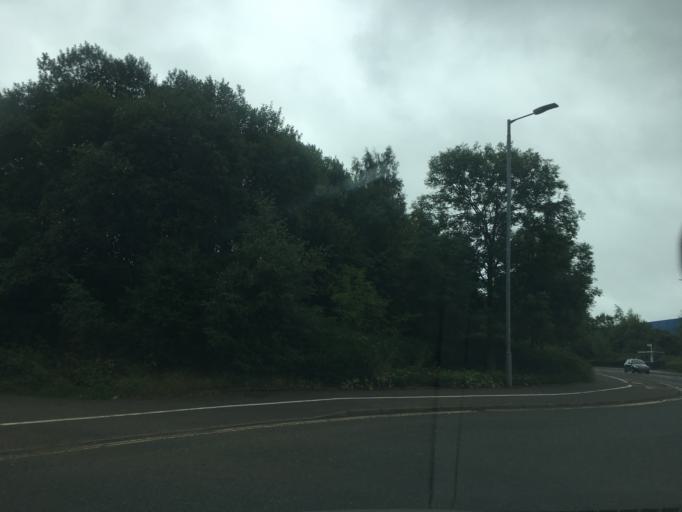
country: GB
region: Scotland
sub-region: Renfrewshire
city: Renfrew
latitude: 55.8710
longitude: -4.3559
